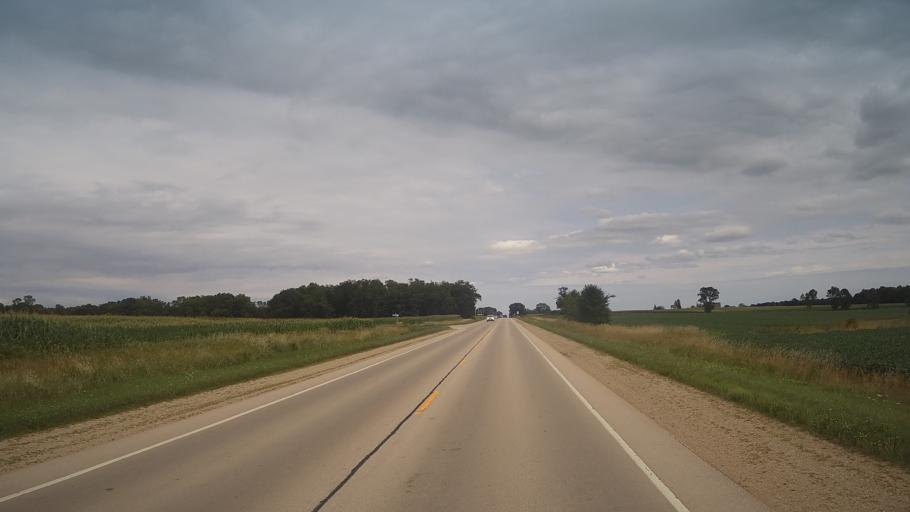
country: US
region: Wisconsin
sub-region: Green Lake County
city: Berlin
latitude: 44.0488
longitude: -88.9478
